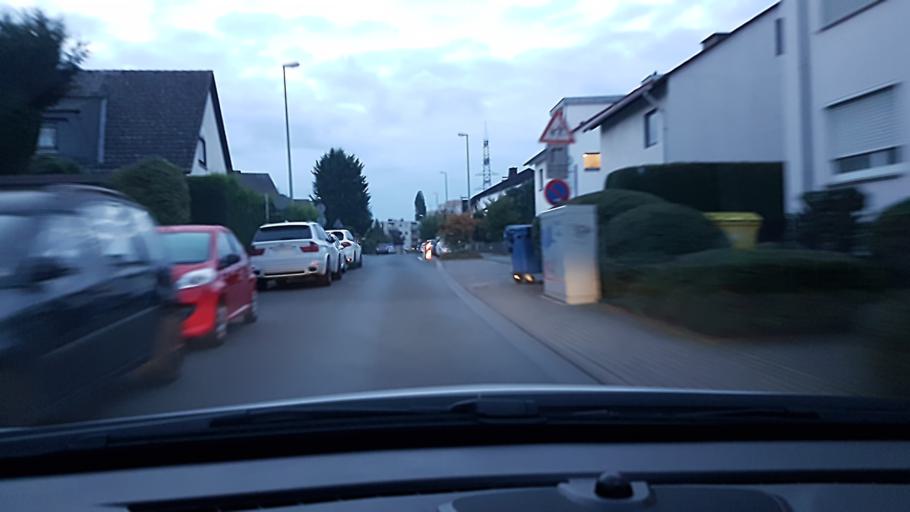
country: DE
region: Hesse
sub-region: Regierungsbezirk Darmstadt
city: Steinbach am Taunus
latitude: 50.1815
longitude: 8.6002
